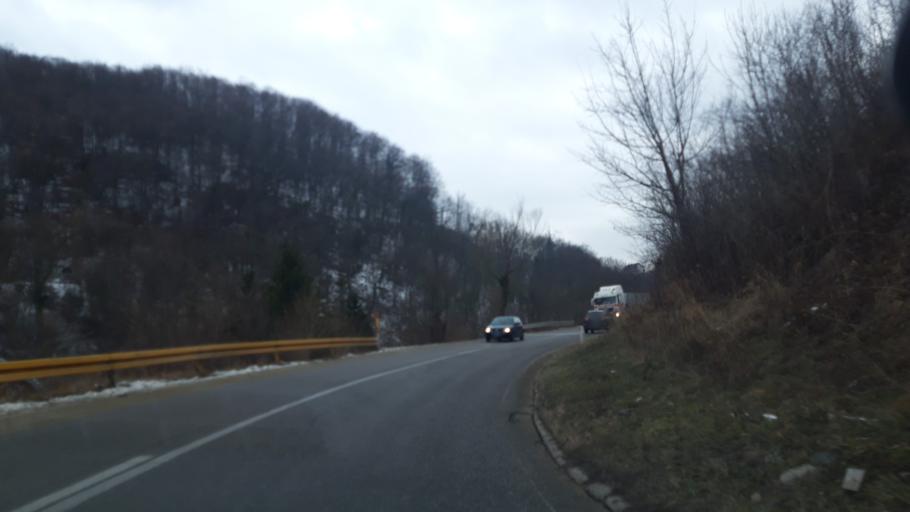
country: BA
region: Republika Srpska
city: Vlasenica
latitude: 44.1815
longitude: 18.9761
